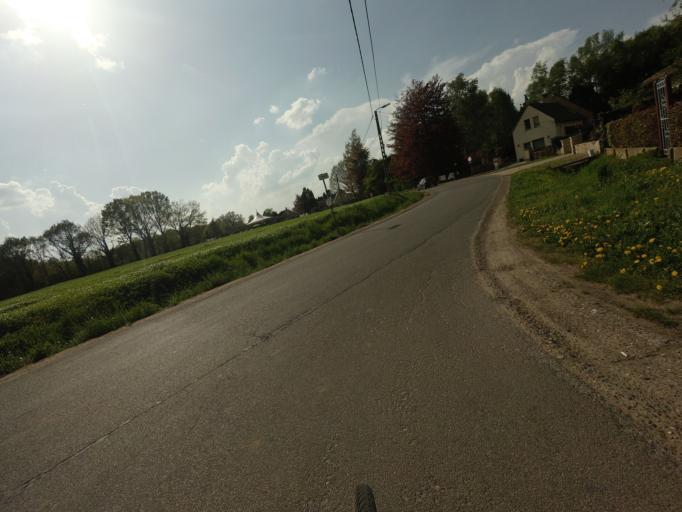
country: BE
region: Flanders
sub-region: Provincie Antwerpen
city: Berlaar
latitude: 51.0766
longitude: 4.6732
